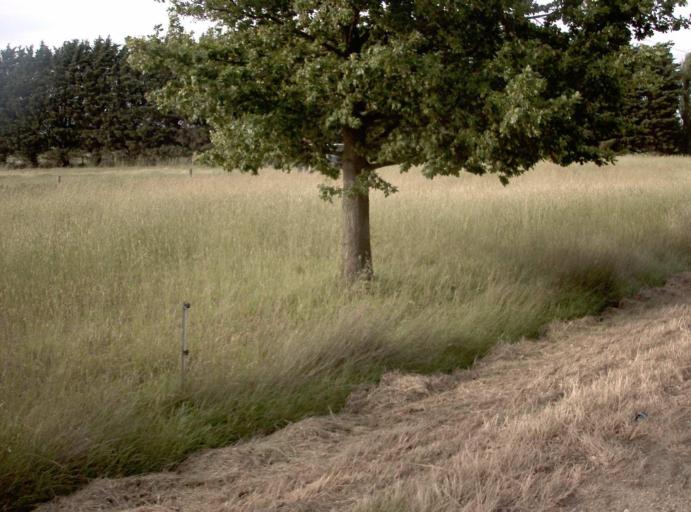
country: AU
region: Victoria
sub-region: Wellington
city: Heyfield
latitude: -38.0114
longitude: 146.7768
